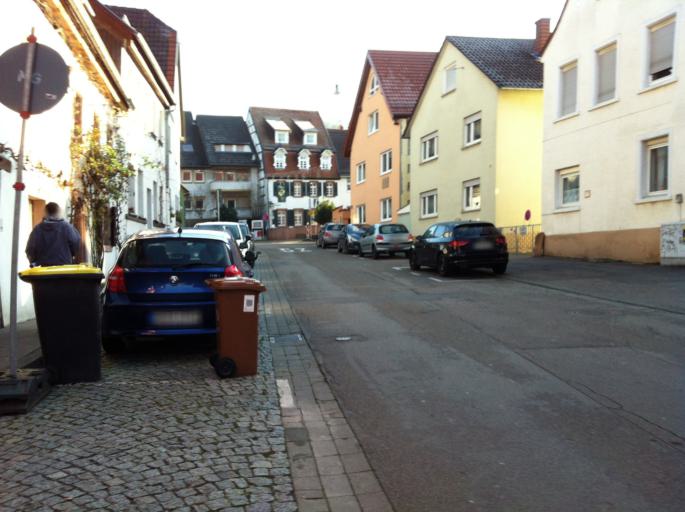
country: DE
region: Baden-Wuerttemberg
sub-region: Karlsruhe Region
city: Heidelberg
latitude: 49.3787
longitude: 8.6924
